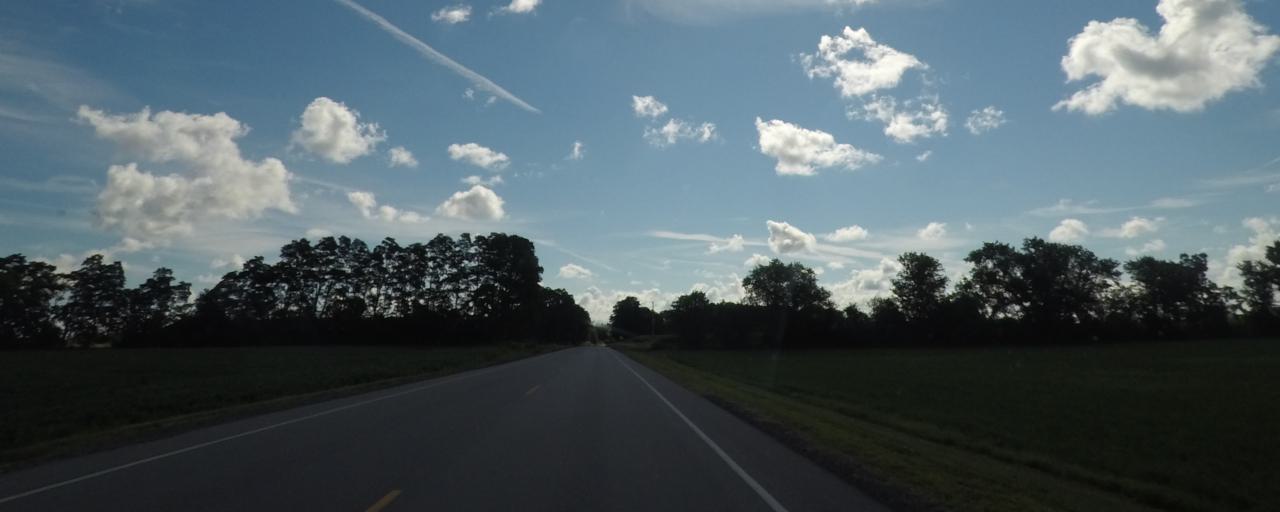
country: US
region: Wisconsin
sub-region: Jefferson County
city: Ixonia
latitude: 43.0758
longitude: -88.5667
